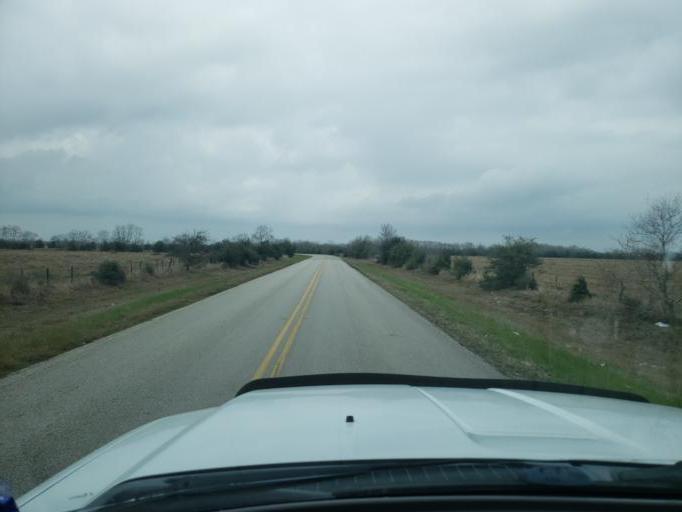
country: US
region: Texas
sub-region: Fort Bend County
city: Needville
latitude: 29.3688
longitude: -95.7280
